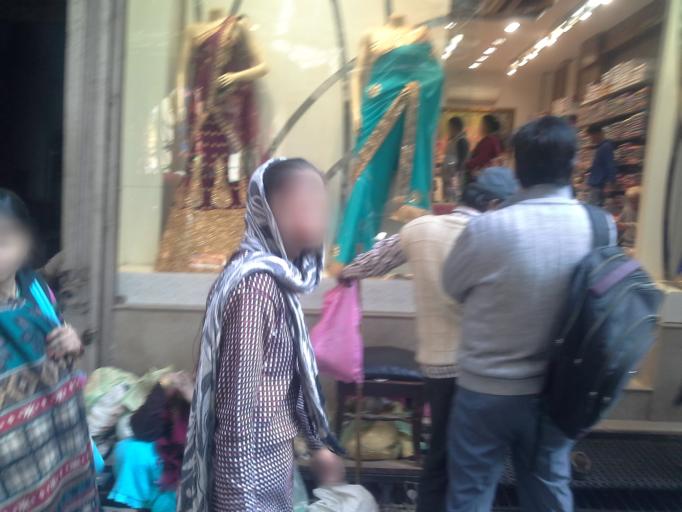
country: IN
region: NCT
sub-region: North Delhi
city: Delhi
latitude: 28.6547
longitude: 77.2283
